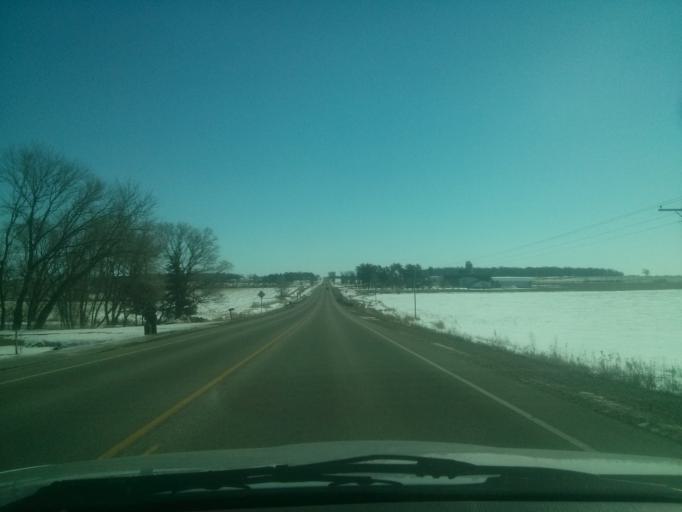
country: US
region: Wisconsin
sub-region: Saint Croix County
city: New Richmond
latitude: 45.1370
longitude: -92.4603
